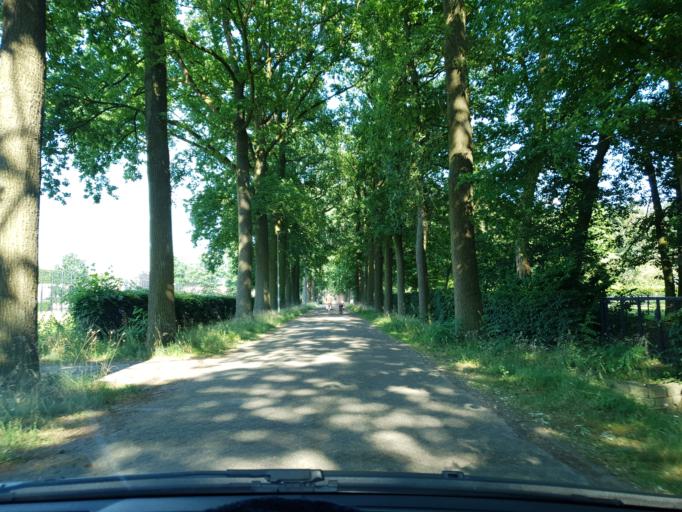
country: BE
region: Flanders
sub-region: Provincie Antwerpen
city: Merksplas
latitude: 51.3543
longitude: 4.8271
